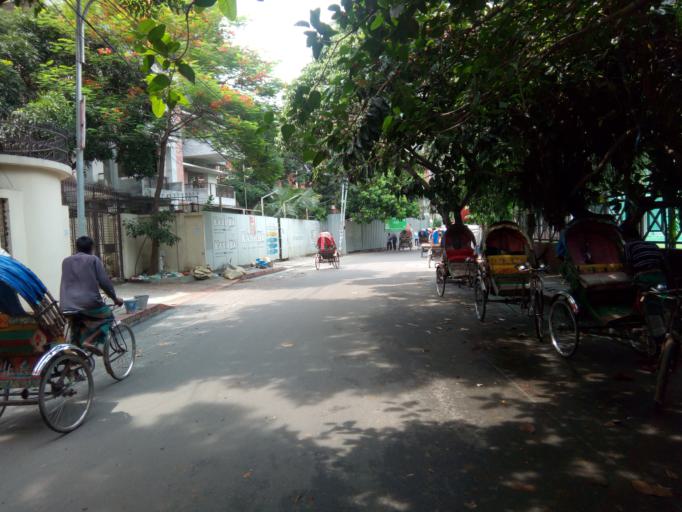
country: BD
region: Dhaka
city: Azimpur
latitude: 23.7461
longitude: 90.3794
